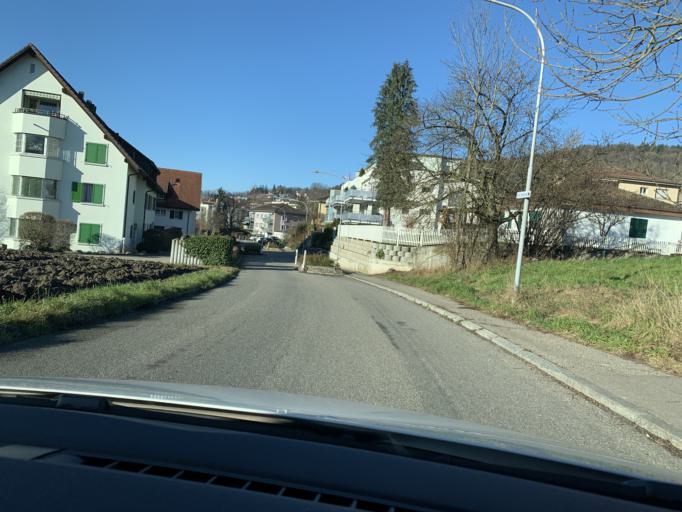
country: CH
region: Zurich
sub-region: Bezirk Dielsdorf
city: Sonnhalde
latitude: 47.4590
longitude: 8.4456
